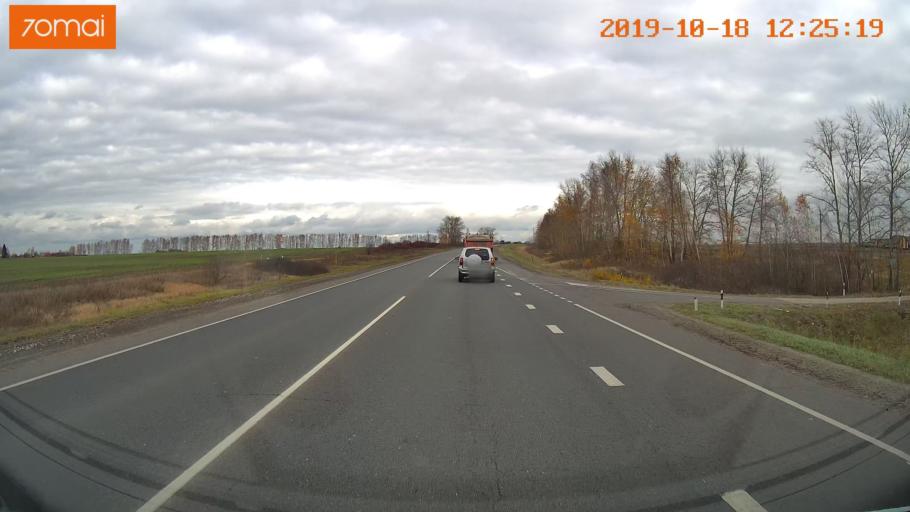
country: RU
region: Rjazan
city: Rybnoye
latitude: 54.5487
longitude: 39.5191
